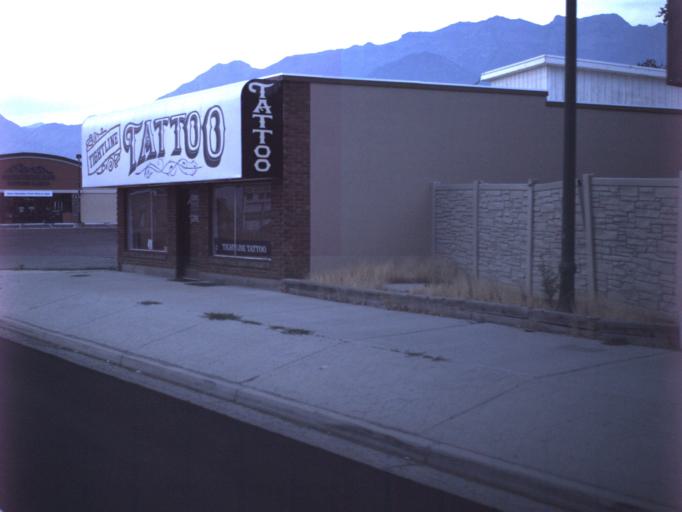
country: US
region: Utah
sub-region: Utah County
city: Orem
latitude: 40.3082
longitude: -111.6997
